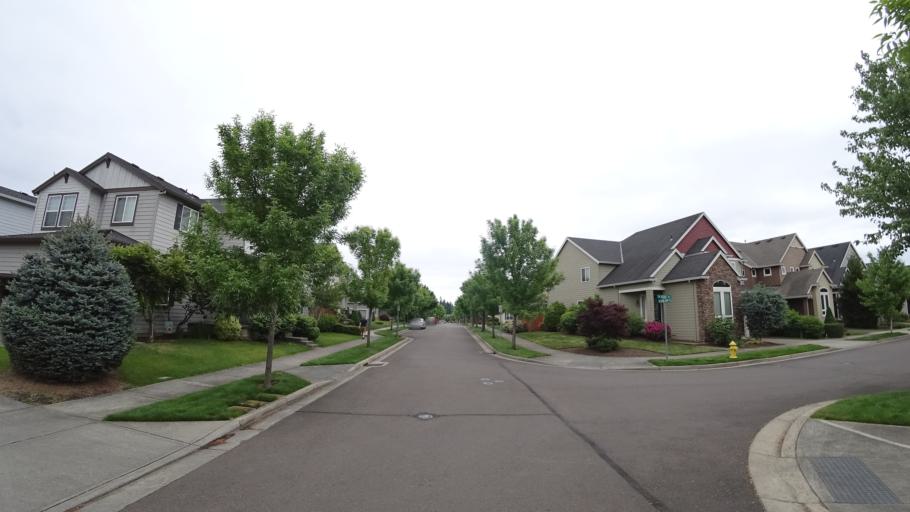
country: US
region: Oregon
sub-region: Washington County
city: Aloha
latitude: 45.4959
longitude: -122.9231
